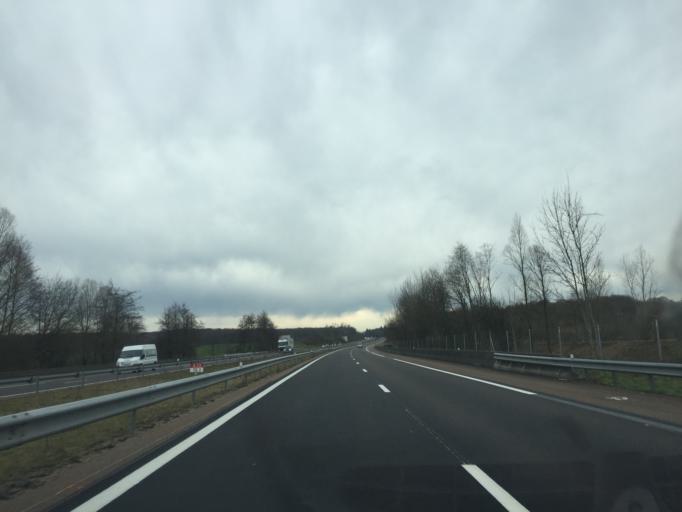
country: FR
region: Franche-Comte
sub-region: Departement du Jura
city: Bletterans
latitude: 46.8029
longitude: 5.5326
